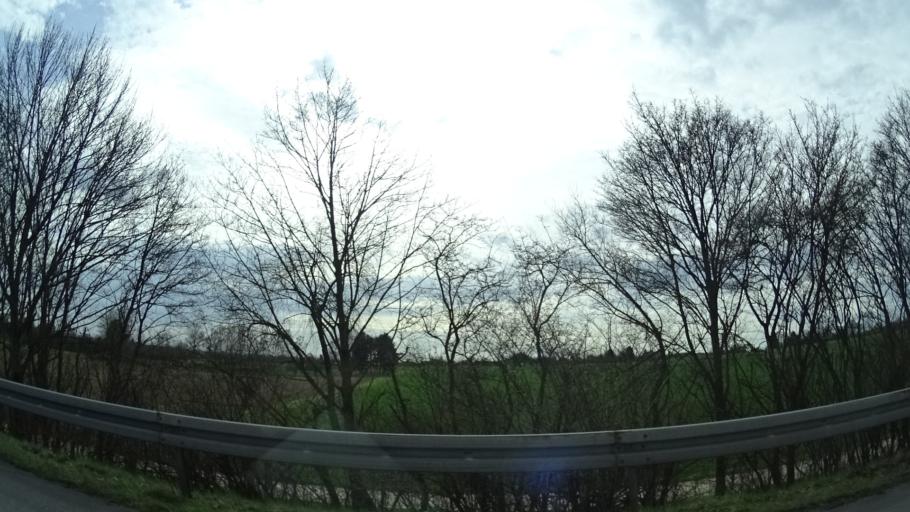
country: DE
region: Hesse
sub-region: Regierungsbezirk Darmstadt
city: Hammersbach
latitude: 50.1945
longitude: 9.0076
